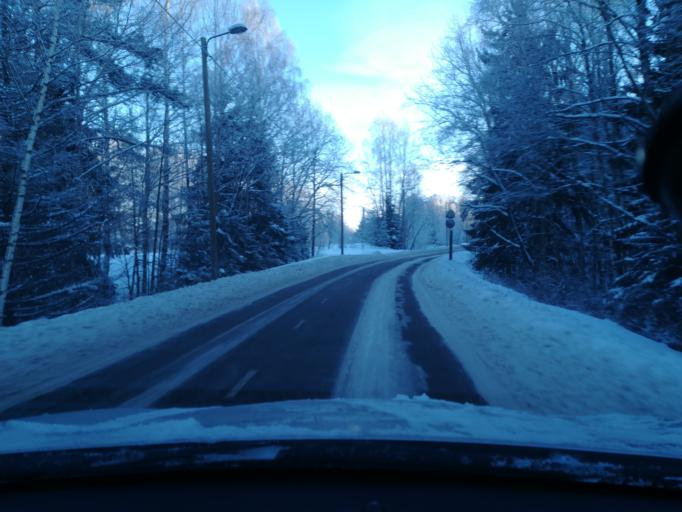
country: EE
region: Harju
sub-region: Saue vald
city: Laagri
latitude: 59.3875
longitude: 24.6250
